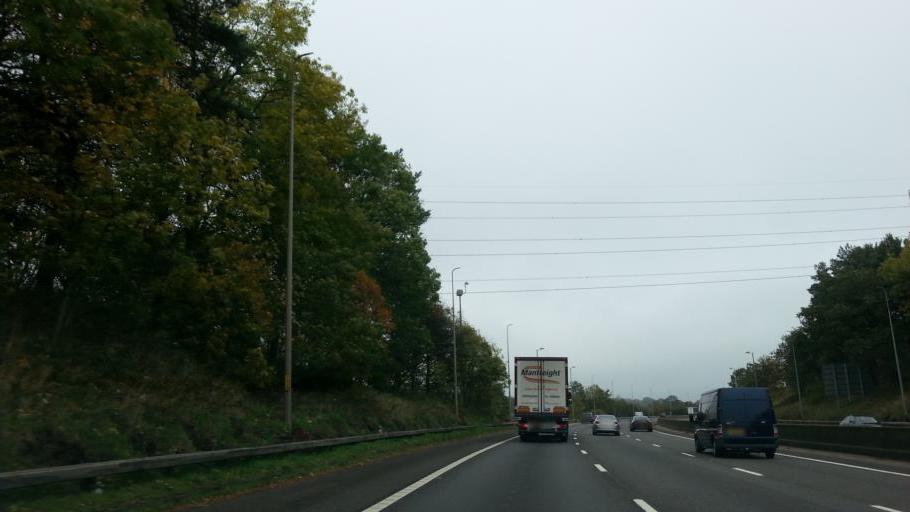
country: GB
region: England
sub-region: Dudley
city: Halesowen
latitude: 52.3943
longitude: -2.0537
